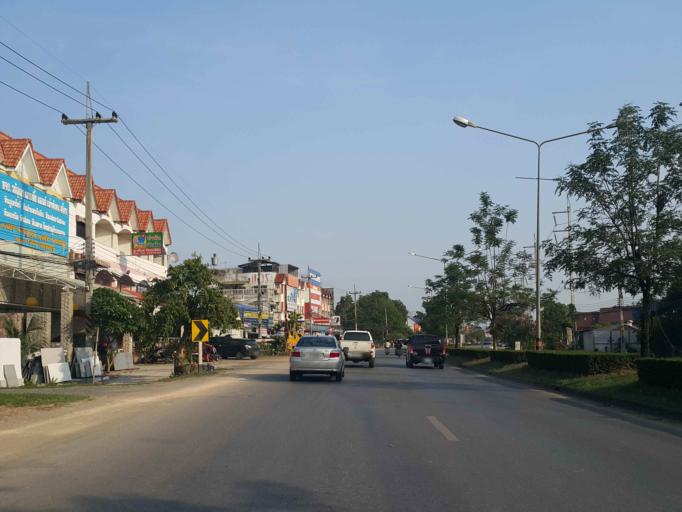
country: TH
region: Chiang Mai
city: San Sai
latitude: 18.8892
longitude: 99.0125
